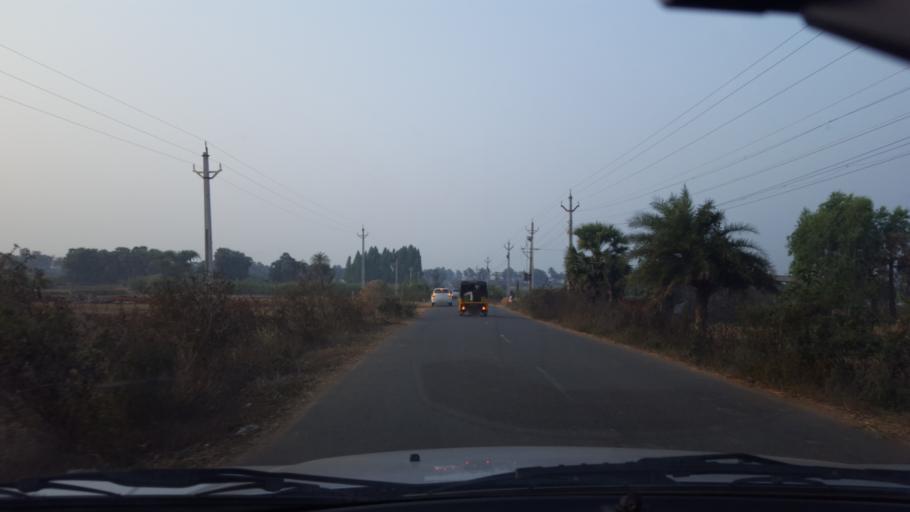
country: IN
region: Andhra Pradesh
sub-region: Srikakulam
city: Amudalavalasa
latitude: 18.3857
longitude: 83.9237
